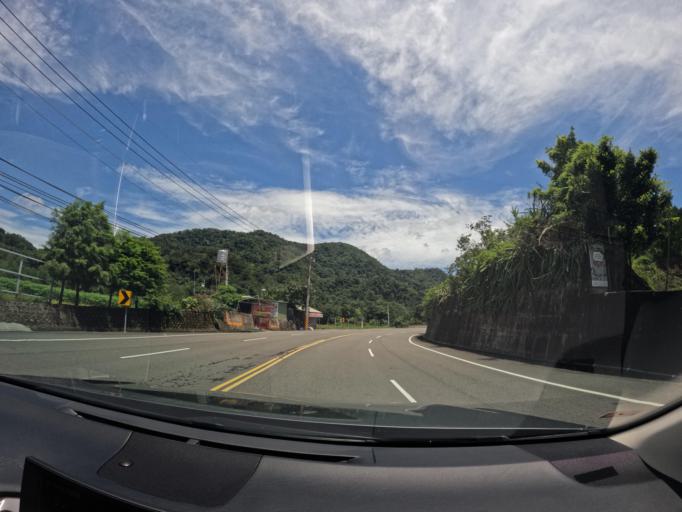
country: TW
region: Taiwan
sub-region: Miaoli
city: Miaoli
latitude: 24.4695
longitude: 120.8867
